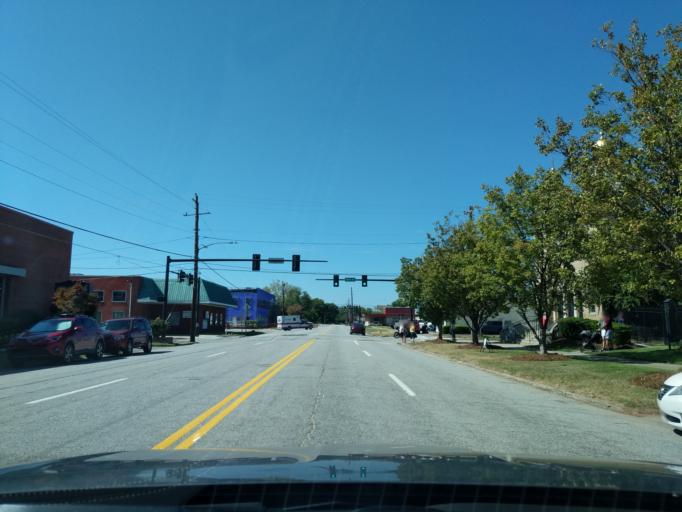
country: US
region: Georgia
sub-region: Richmond County
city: Augusta
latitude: 33.4734
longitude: -81.9707
